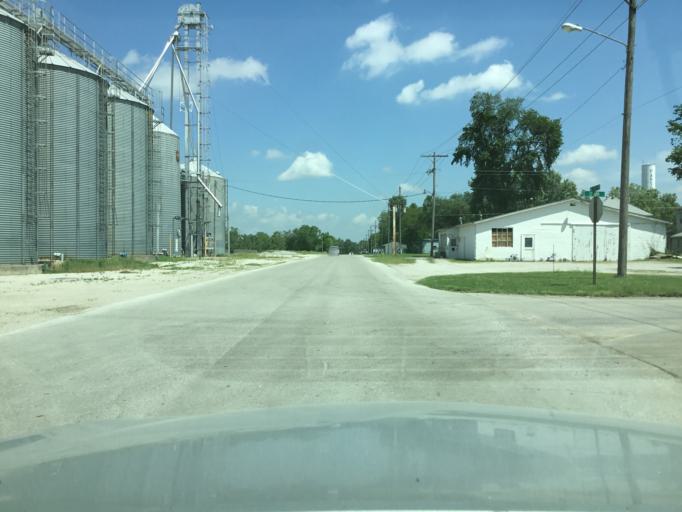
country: US
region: Kansas
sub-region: Labette County
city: Parsons
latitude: 37.3435
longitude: -95.2657
